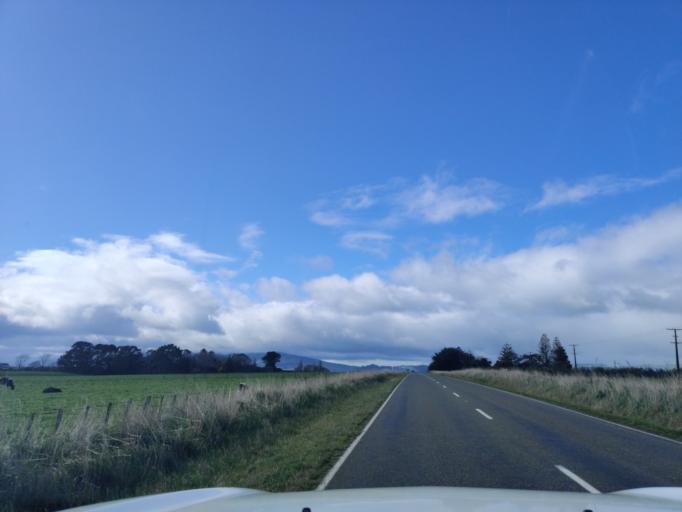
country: NZ
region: Manawatu-Wanganui
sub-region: Palmerston North City
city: Palmerston North
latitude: -40.2879
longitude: 175.6814
